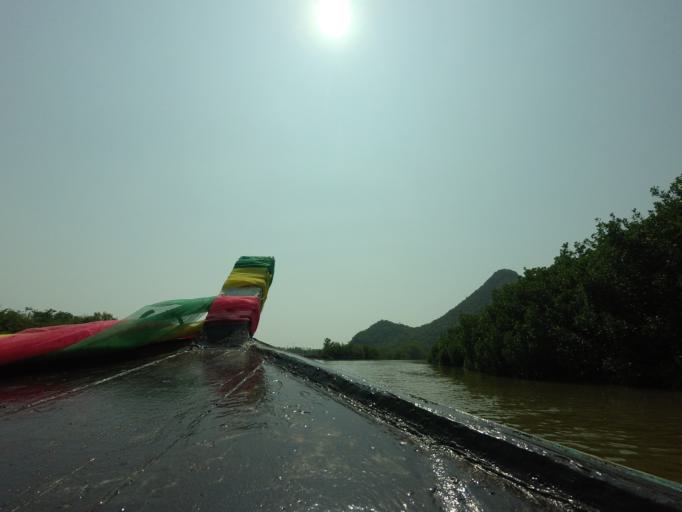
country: TH
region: Prachuap Khiri Khan
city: Kui Buri
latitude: 12.1375
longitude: 99.9611
